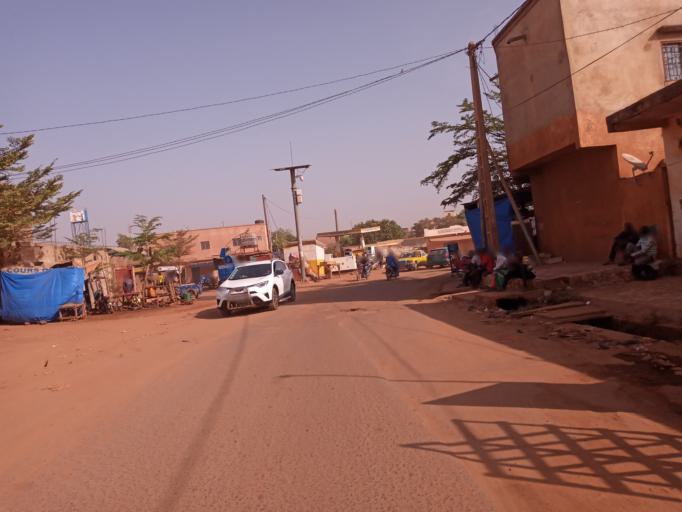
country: ML
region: Bamako
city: Bamako
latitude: 12.5849
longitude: -7.9590
